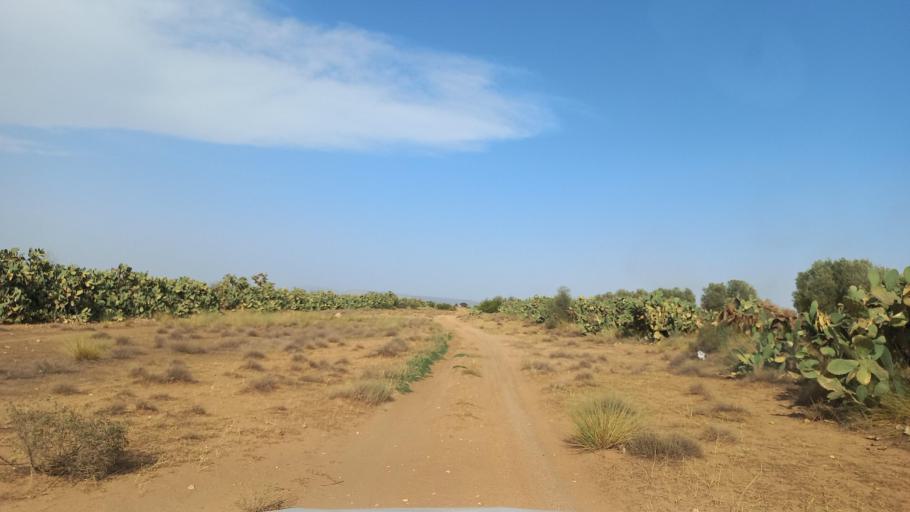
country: TN
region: Al Qasrayn
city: Kasserine
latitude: 35.2198
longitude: 8.9557
